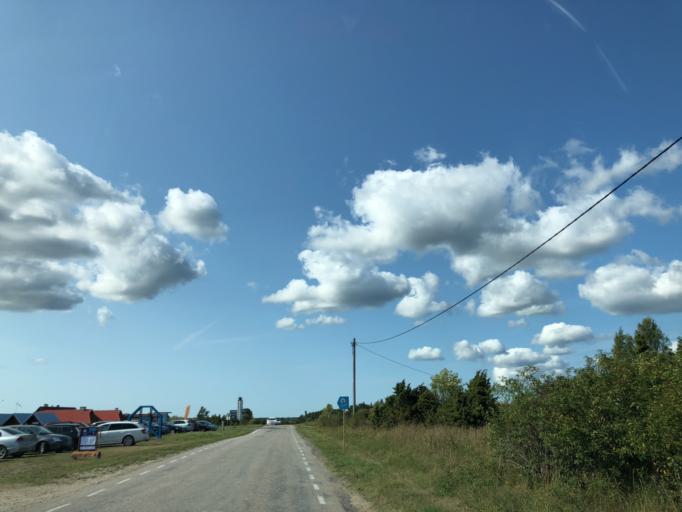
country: EE
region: Hiiumaa
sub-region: Kaerdla linn
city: Kardla
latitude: 58.7888
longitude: 22.7743
